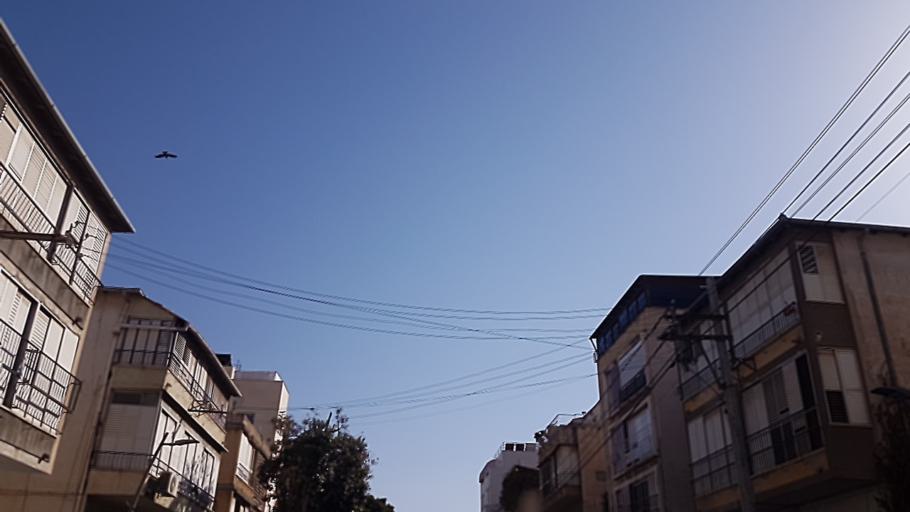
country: IL
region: Tel Aviv
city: Giv`atayim
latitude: 32.0759
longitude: 34.8231
